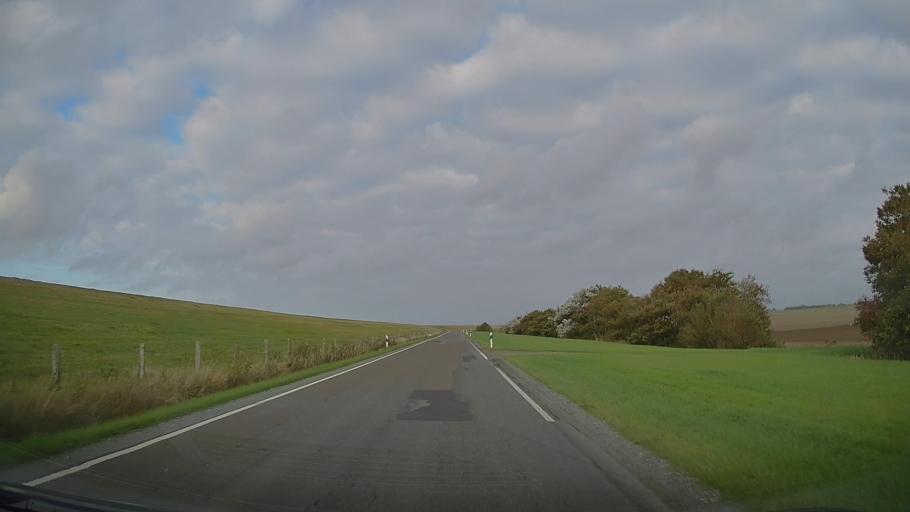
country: DE
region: Schleswig-Holstein
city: Uelvesbull
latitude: 54.4059
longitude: 8.8767
